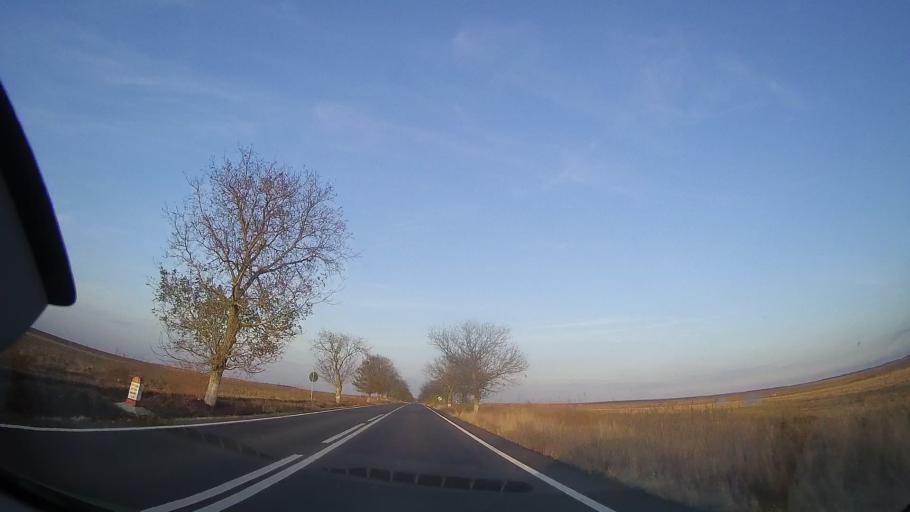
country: RO
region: Constanta
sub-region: Comuna Amzacea
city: Amzacea
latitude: 43.9383
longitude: 28.3683
